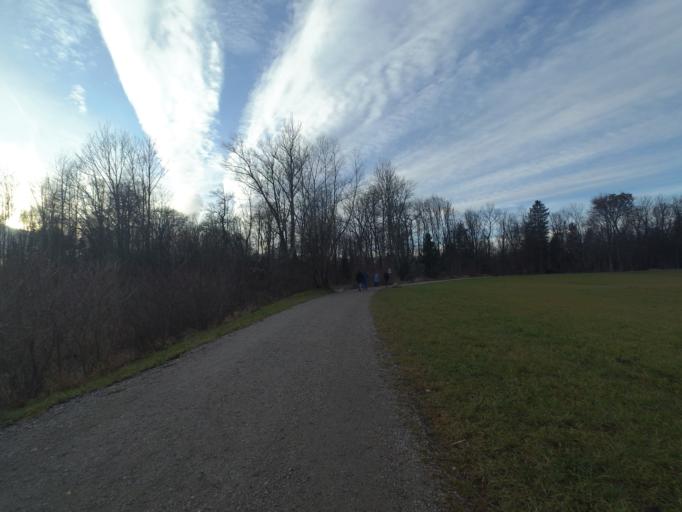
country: DE
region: Bavaria
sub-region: Upper Bavaria
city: Freilassing
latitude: 47.8234
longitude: 12.9848
